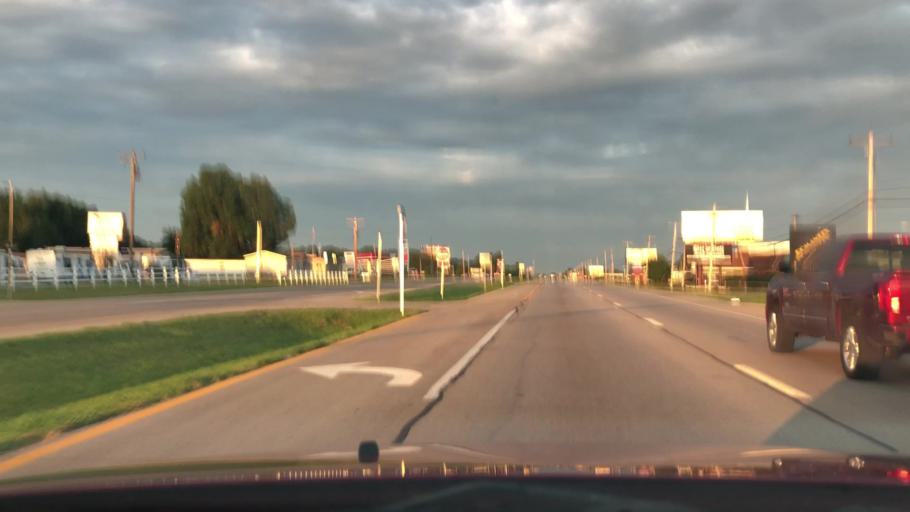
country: US
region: Missouri
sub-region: Greene County
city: Springfield
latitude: 37.1828
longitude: -93.3436
